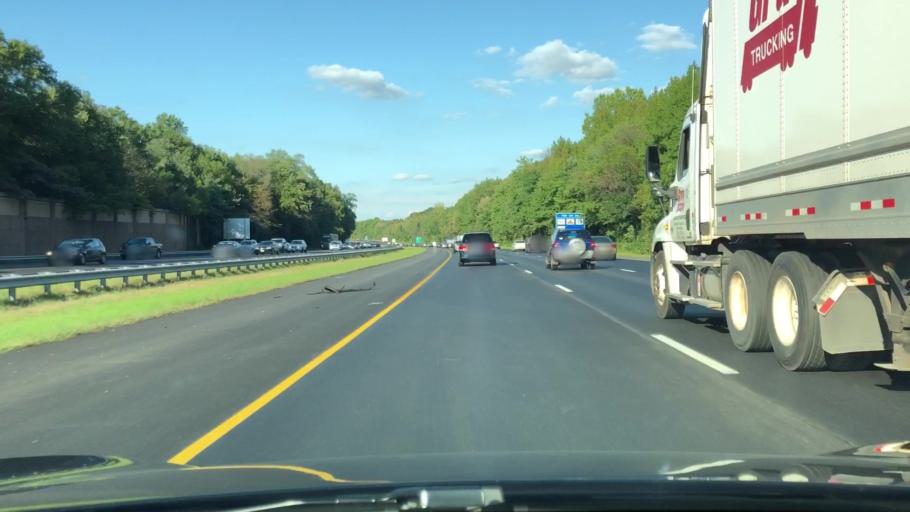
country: US
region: New Jersey
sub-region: Camden County
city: Ellisburg
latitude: 39.8963
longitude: -74.9922
